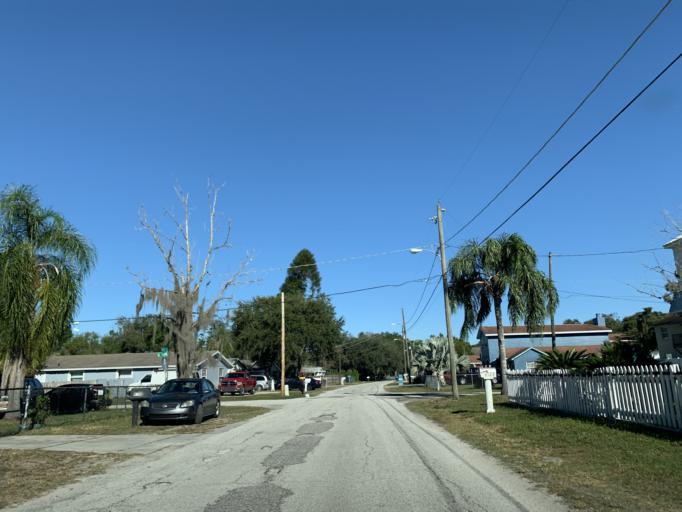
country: US
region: Florida
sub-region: Hillsborough County
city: Temple Terrace
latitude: 28.0236
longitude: -82.4172
